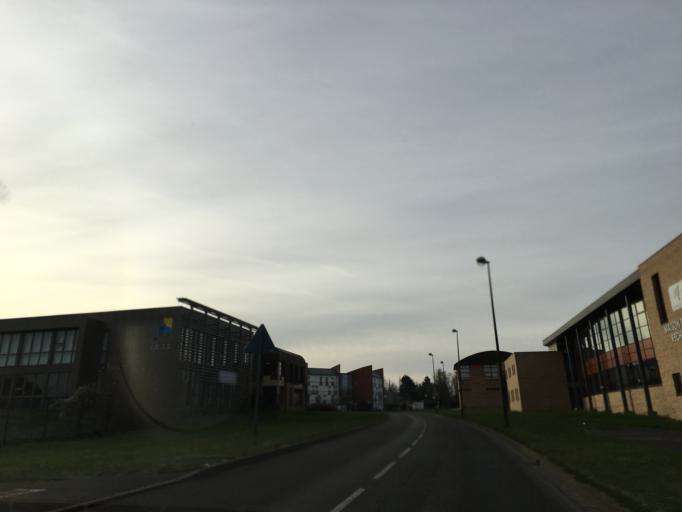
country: FR
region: Nord-Pas-de-Calais
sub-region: Departement du Pas-de-Calais
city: Saint-Laurent-Blangy
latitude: 50.2840
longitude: 2.7955
